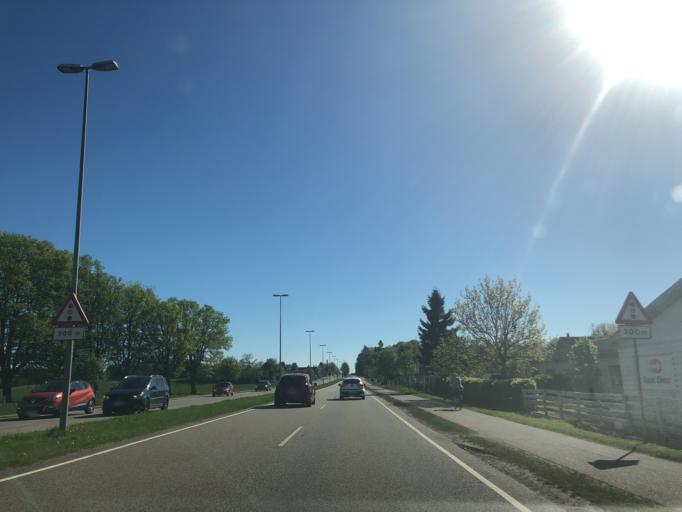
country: DK
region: Zealand
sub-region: Koge Kommune
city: Koge
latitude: 55.4251
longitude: 12.1497
